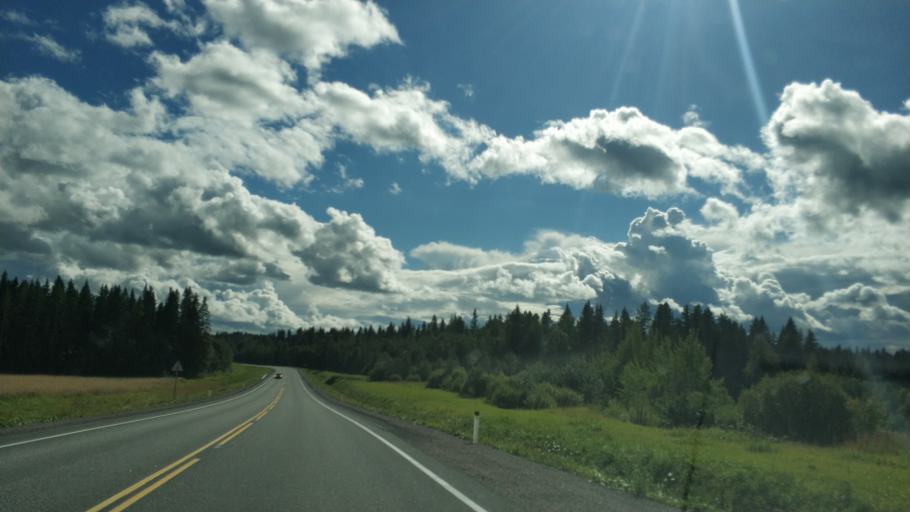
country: RU
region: Republic of Karelia
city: Ruskeala
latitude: 61.8813
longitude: 30.6436
